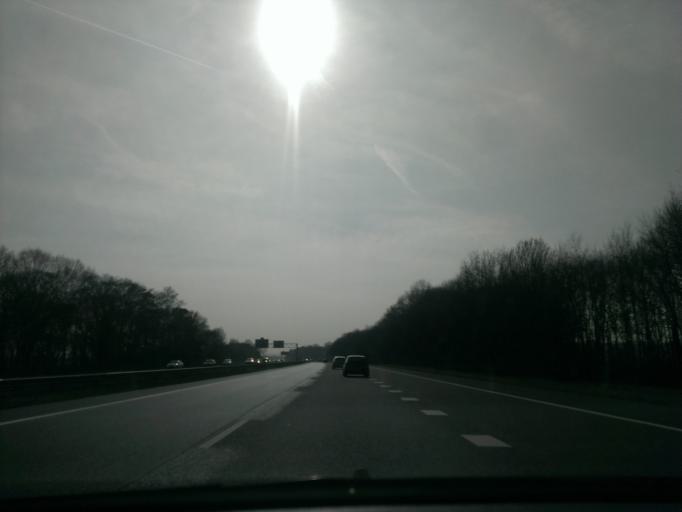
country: NL
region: Overijssel
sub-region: Gemeente Hof van Twente
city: Delden
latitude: 52.3081
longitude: 6.6869
